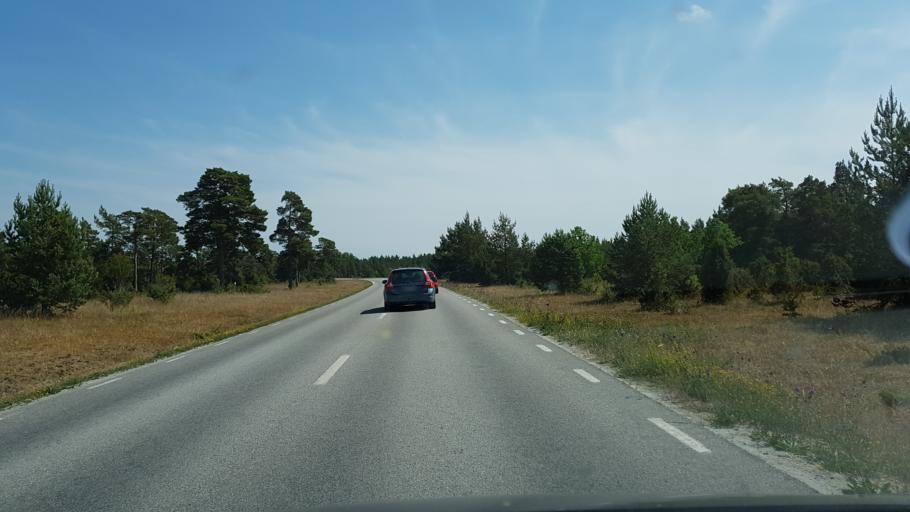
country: SE
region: Gotland
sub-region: Gotland
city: Visby
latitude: 57.6349
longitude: 18.4055
